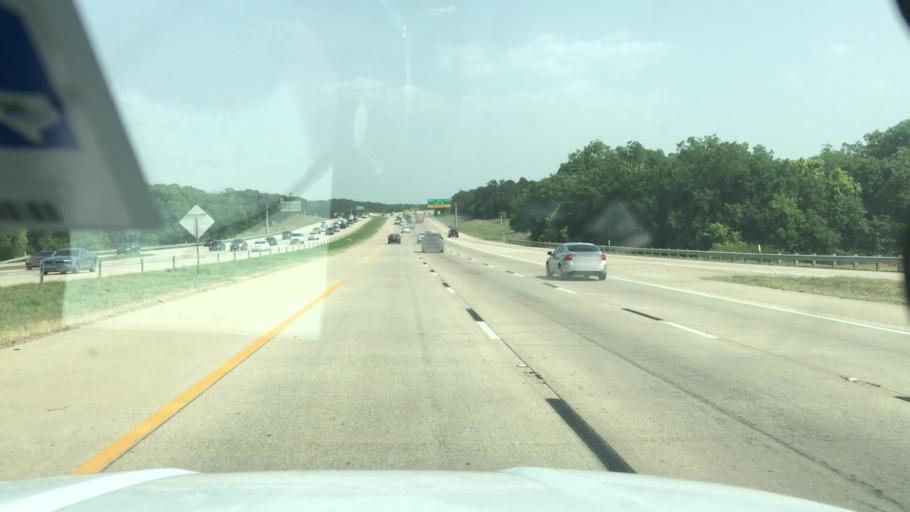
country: US
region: Texas
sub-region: Denton County
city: Trophy Club
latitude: 32.9805
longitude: -97.1662
